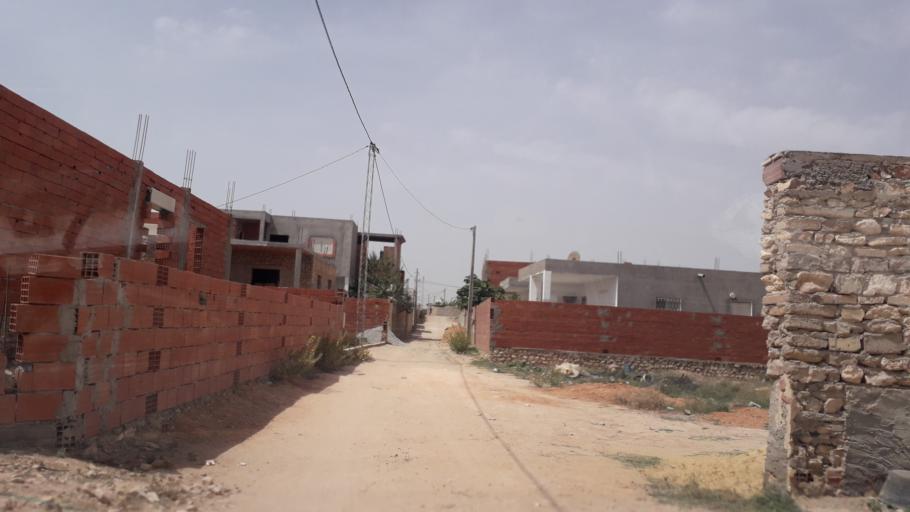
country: TN
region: Safaqis
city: Al Qarmadah
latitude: 34.8449
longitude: 10.7790
